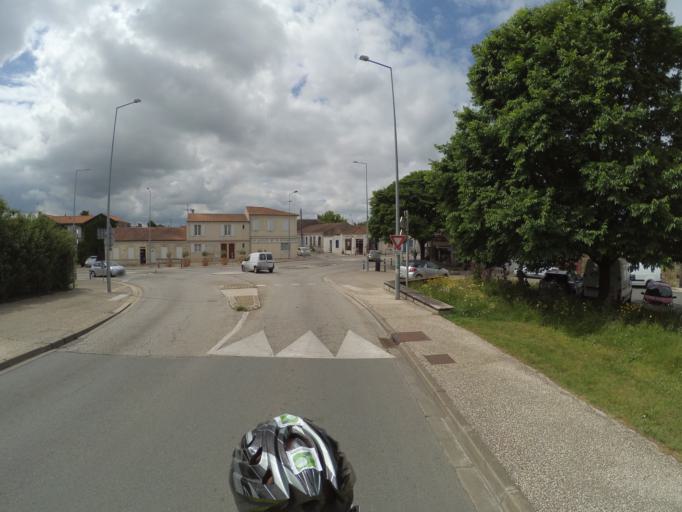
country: FR
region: Poitou-Charentes
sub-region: Departement de la Charente-Maritime
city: Rochefort
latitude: 45.9477
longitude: -0.9679
